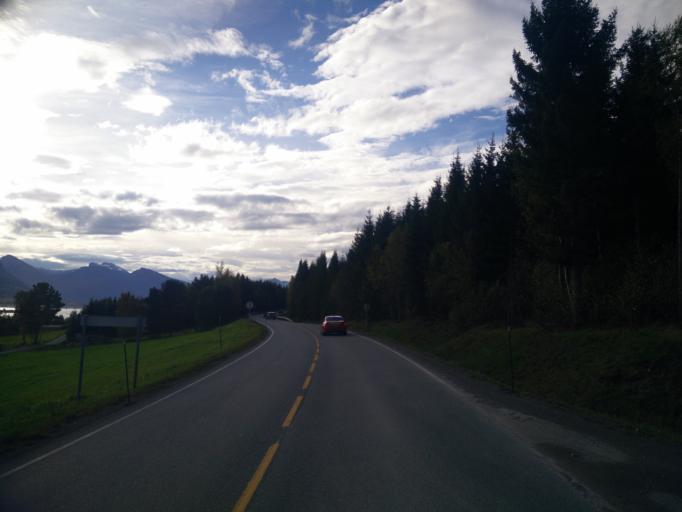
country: NO
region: More og Romsdal
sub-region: Vestnes
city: Vestnes
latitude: 62.6459
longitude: 7.0812
